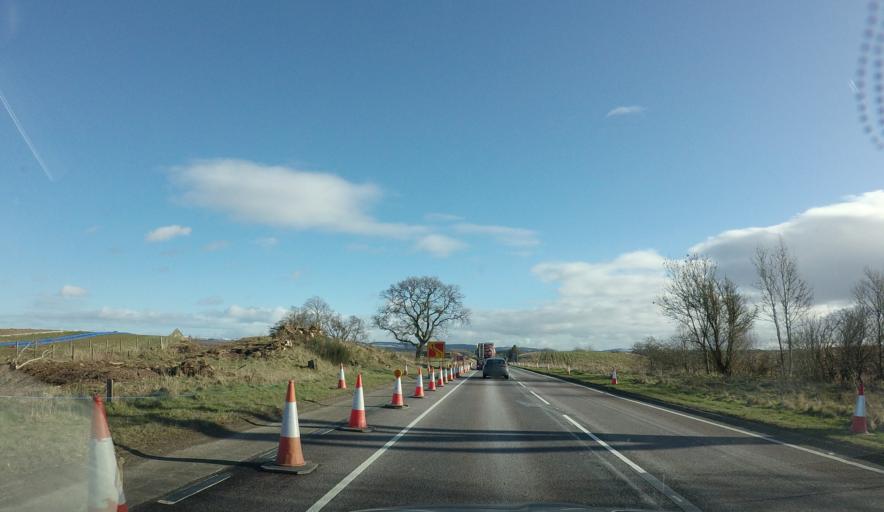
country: GB
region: Scotland
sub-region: Perth and Kinross
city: Bankfoot
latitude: 56.4769
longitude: -3.4898
